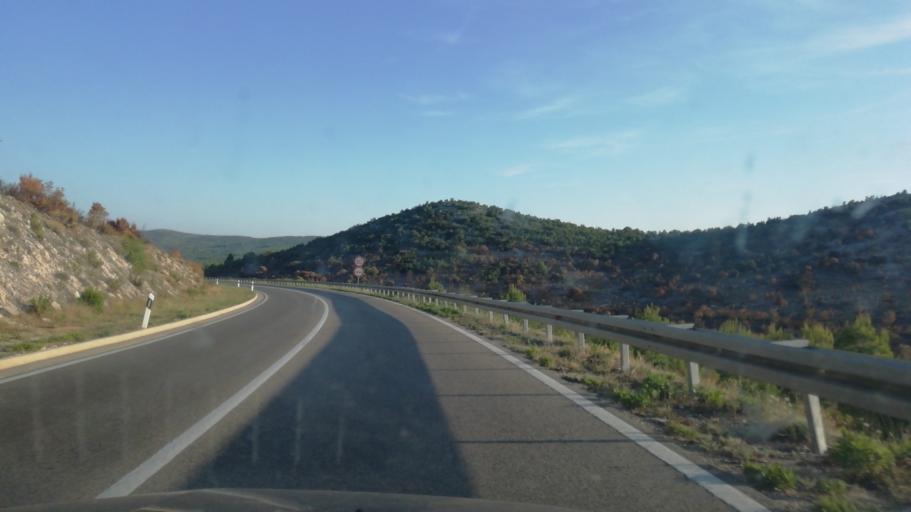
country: HR
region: Sibensko-Kniniska
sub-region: Grad Sibenik
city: Sibenik
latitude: 43.7534
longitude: 15.9363
